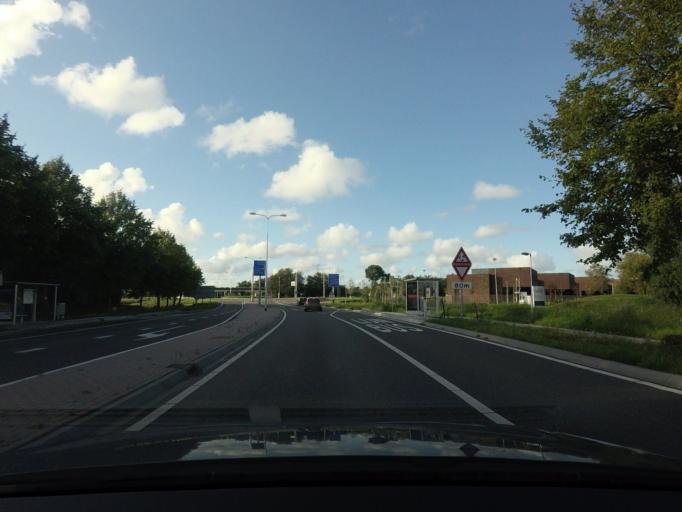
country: NL
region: South Holland
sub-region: Gemeente Teylingen
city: Voorhout
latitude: 52.2023
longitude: 4.4851
